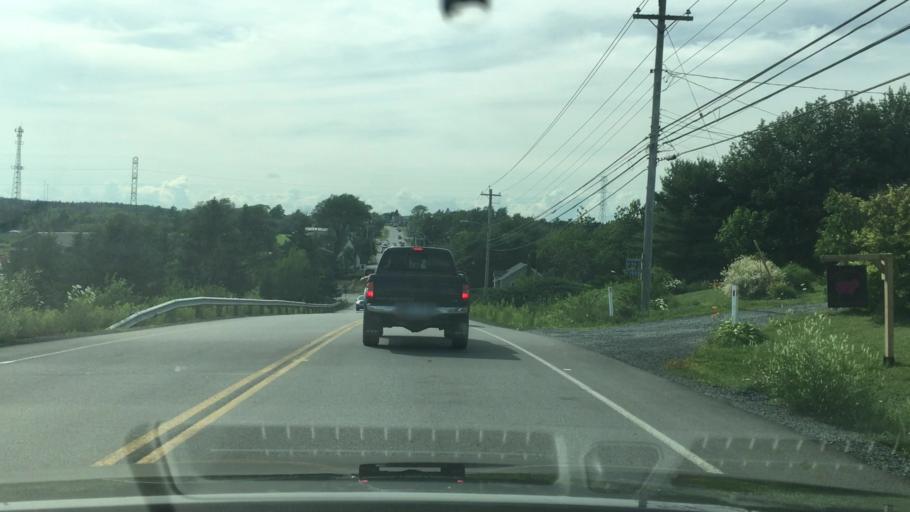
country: CA
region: Nova Scotia
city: Dartmouth
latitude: 44.7310
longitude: -63.7550
